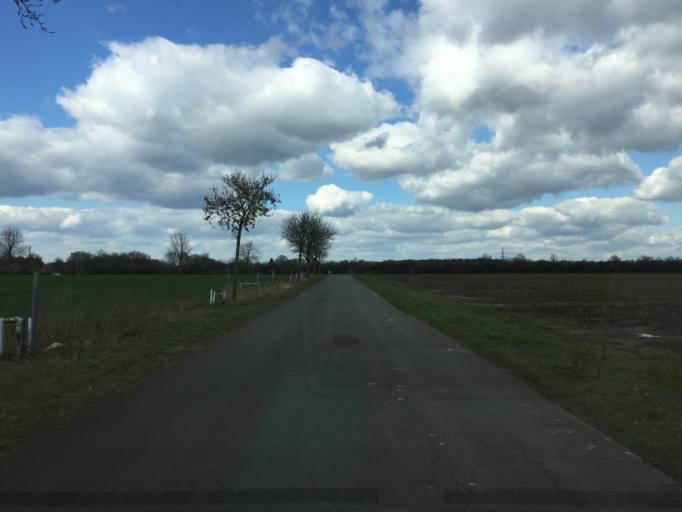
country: DE
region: Lower Saxony
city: Sulingen
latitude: 52.6664
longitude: 8.8131
